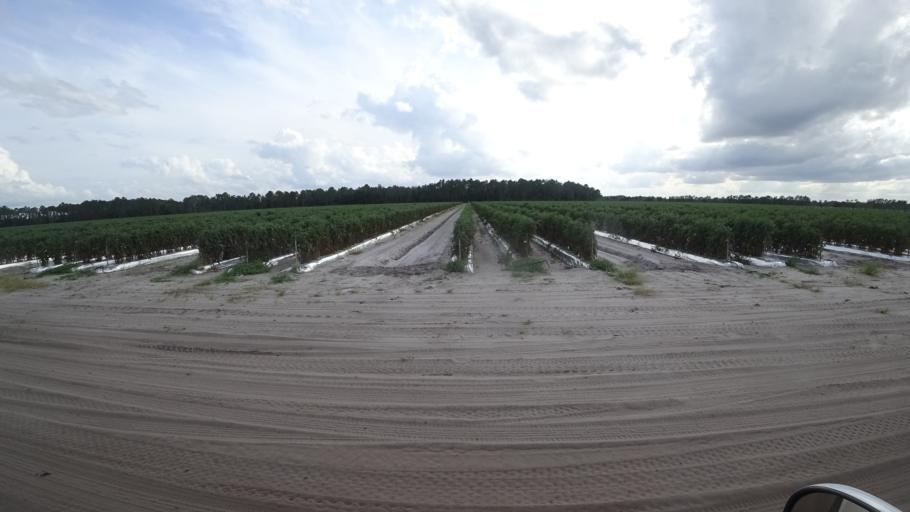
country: US
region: Florida
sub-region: Hillsborough County
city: Balm
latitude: 27.6237
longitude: -82.1325
